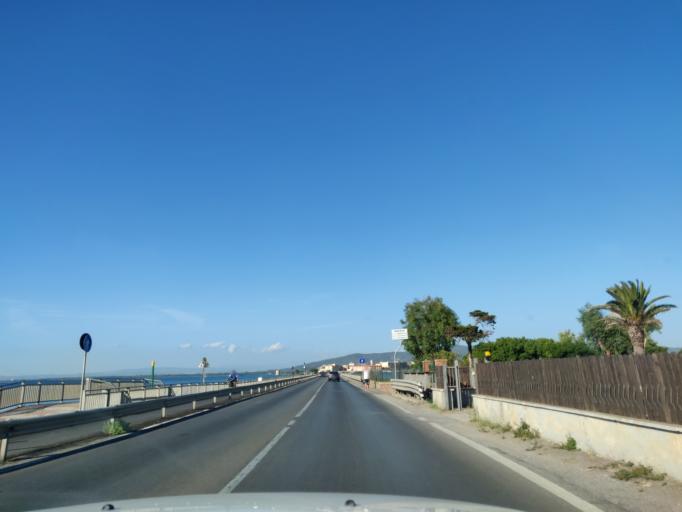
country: IT
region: Tuscany
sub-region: Provincia di Grosseto
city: Orbetello
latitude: 42.4288
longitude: 11.1991
